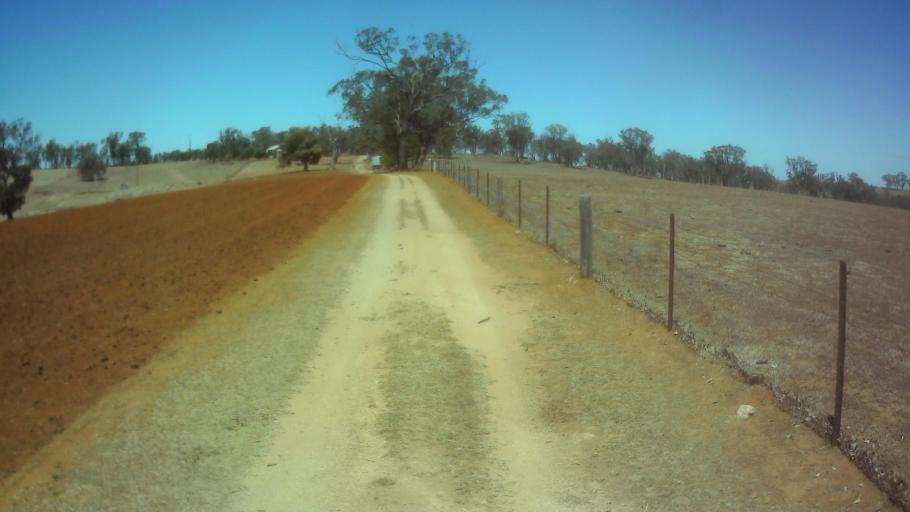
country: AU
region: New South Wales
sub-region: Cowra
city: Cowra
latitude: -33.9069
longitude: 148.5075
